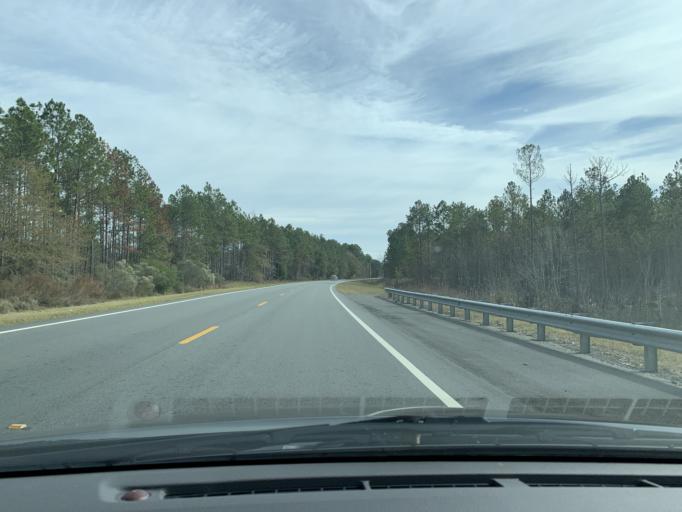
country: US
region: Georgia
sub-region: Wilcox County
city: Rochelle
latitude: 31.9596
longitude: -83.5873
